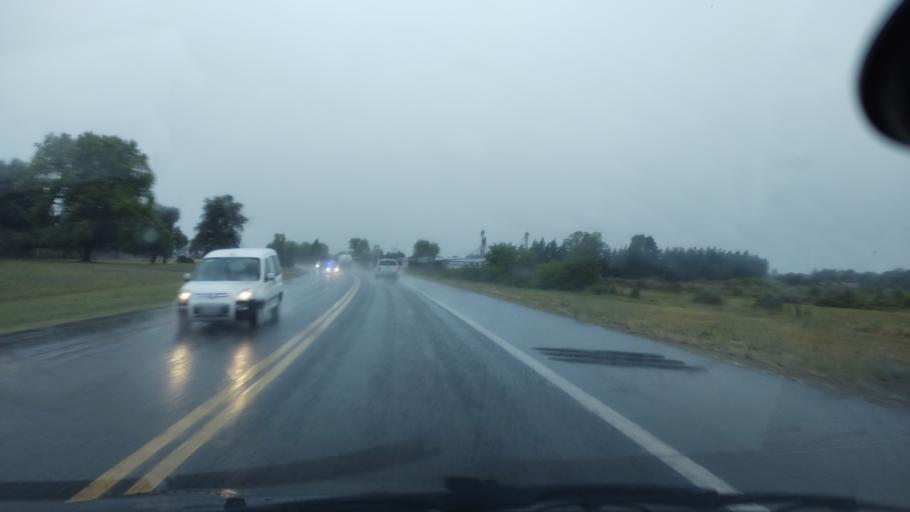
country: AR
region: Buenos Aires
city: Canuelas
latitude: -35.0527
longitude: -58.7765
